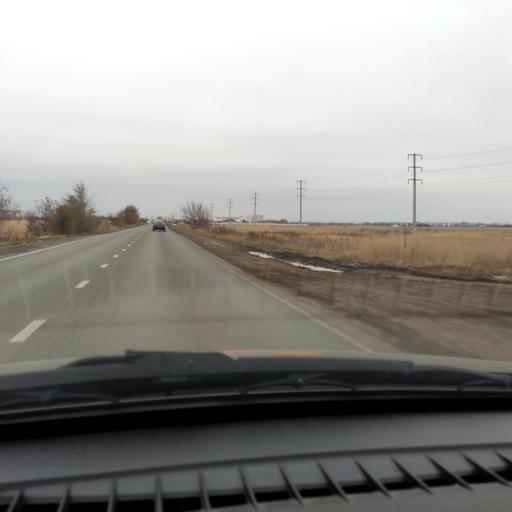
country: RU
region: Samara
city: Podstepki
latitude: 53.5198
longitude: 49.2052
